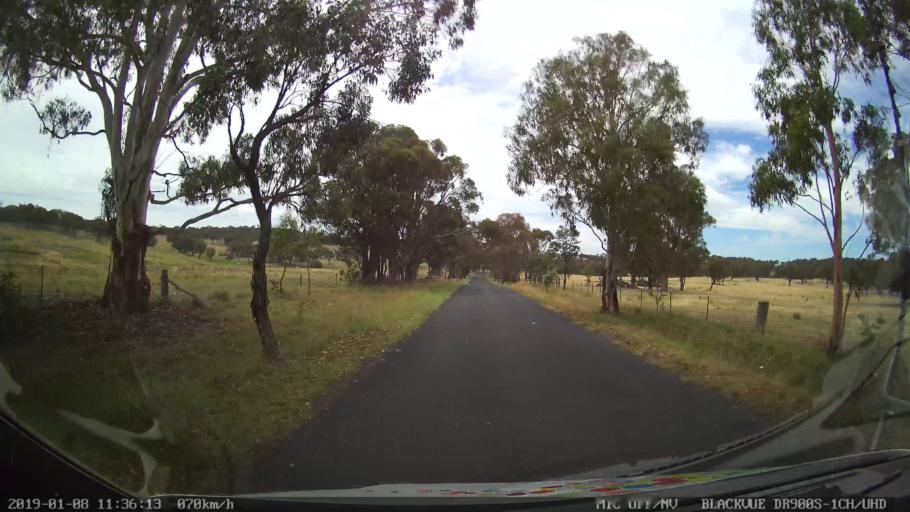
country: AU
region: New South Wales
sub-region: Guyra
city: Guyra
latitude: -30.3439
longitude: 151.5419
